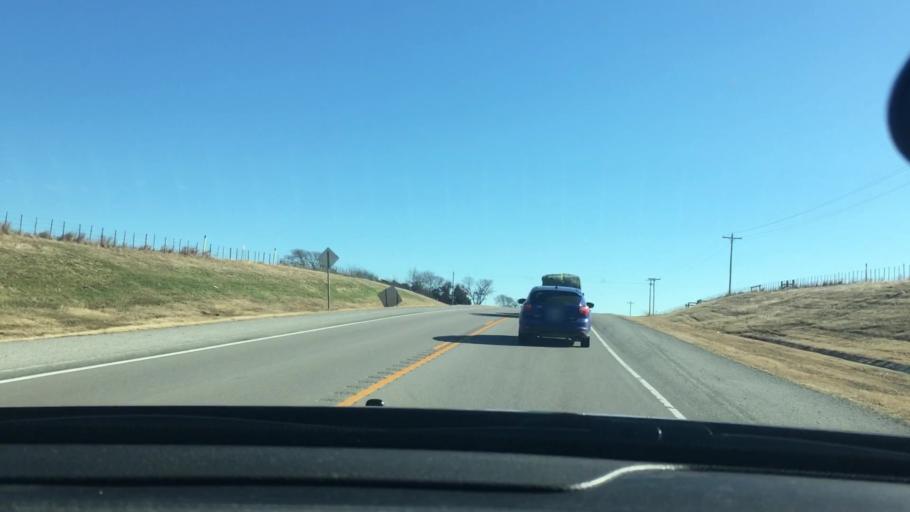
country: US
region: Oklahoma
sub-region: Love County
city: Marietta
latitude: 33.9403
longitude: -97.2066
